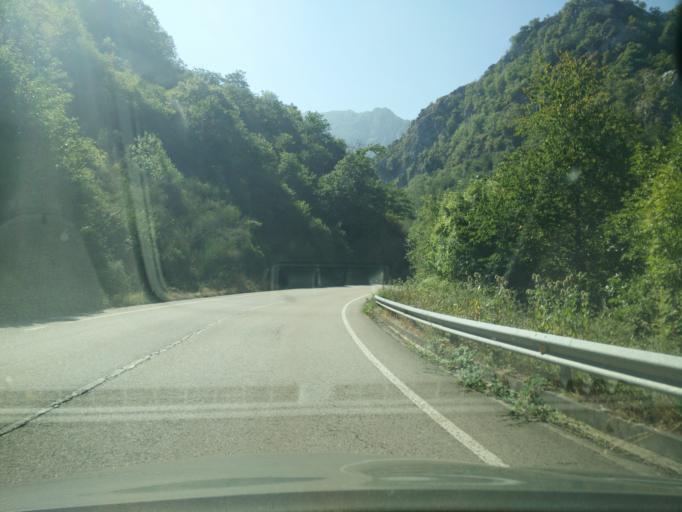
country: ES
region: Asturias
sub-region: Province of Asturias
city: Campo de Caso
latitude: 43.1834
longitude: -5.3663
